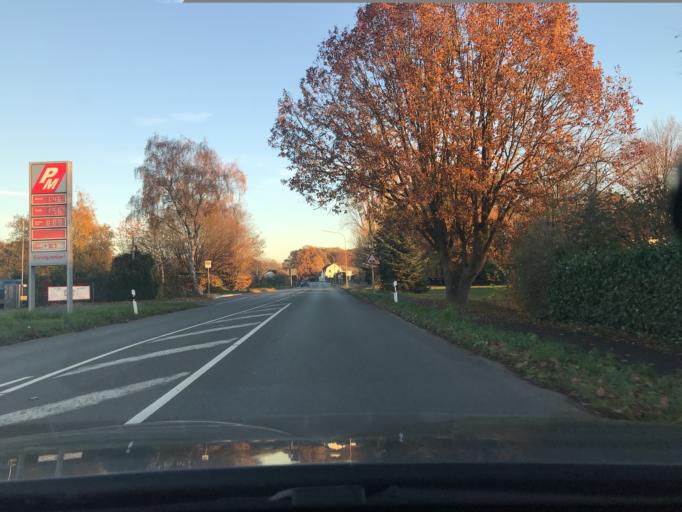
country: DE
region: North Rhine-Westphalia
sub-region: Regierungsbezirk Dusseldorf
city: Rheurdt
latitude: 51.4410
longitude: 6.4915
